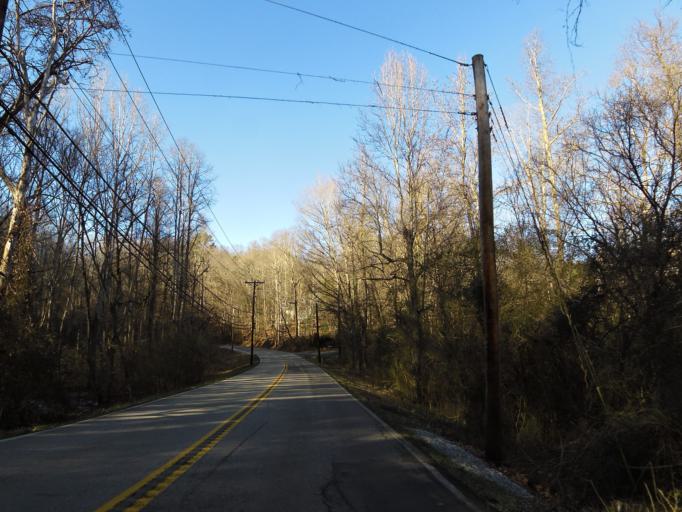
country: US
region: Tennessee
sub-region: Knox County
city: Knoxville
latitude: 35.9047
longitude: -83.9803
